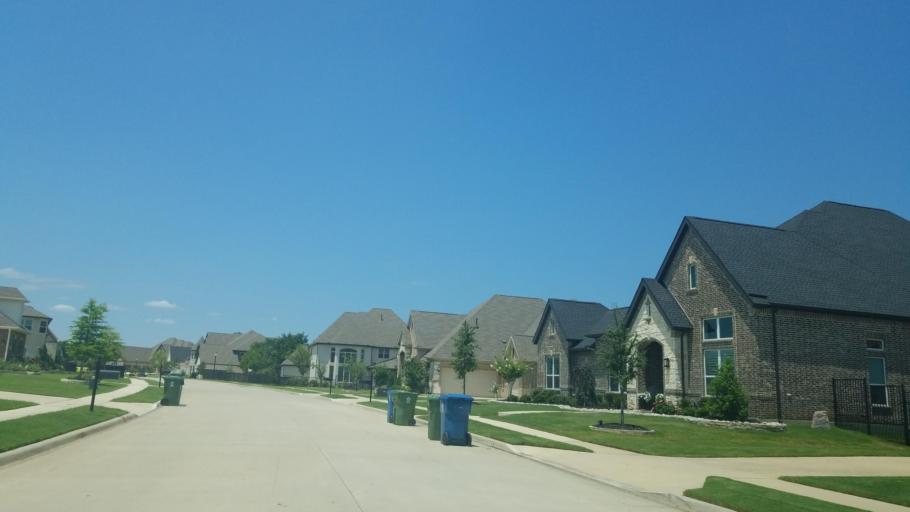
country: US
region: Texas
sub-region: Denton County
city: Copper Canyon
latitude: 33.0766
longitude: -97.0920
